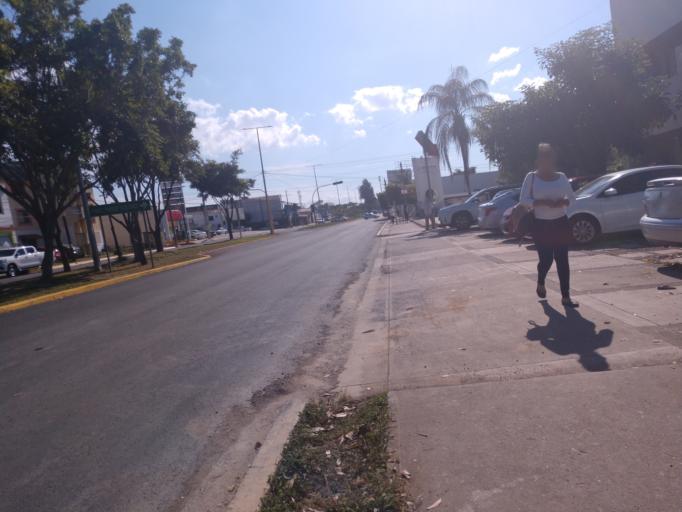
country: MX
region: Nayarit
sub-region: Tepic
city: La Corregidora
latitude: 21.4764
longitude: -104.8525
